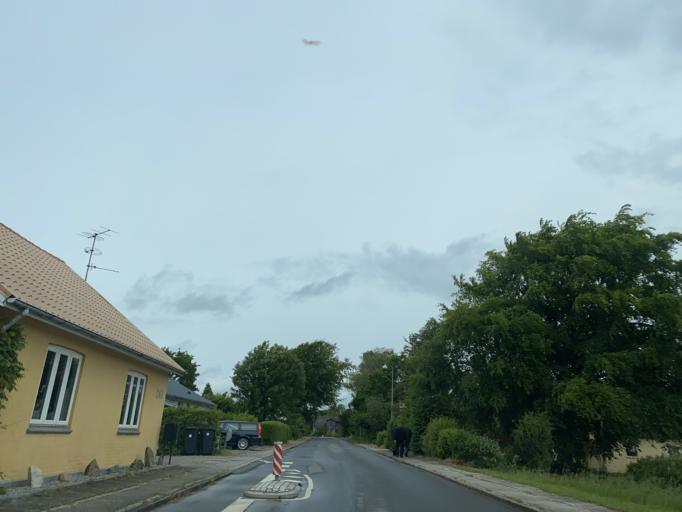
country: DK
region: Central Jutland
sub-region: Favrskov Kommune
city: Hammel
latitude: 56.2401
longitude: 9.8154
